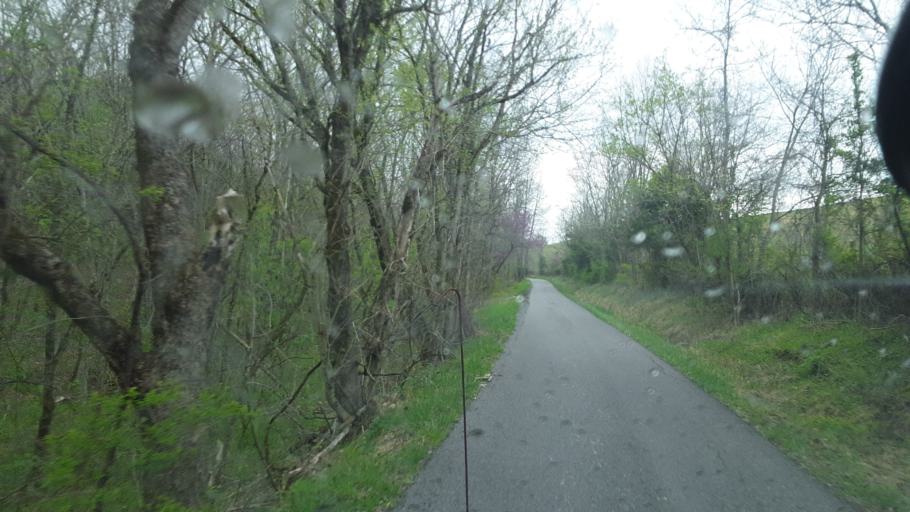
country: US
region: Kentucky
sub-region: Owen County
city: Owenton
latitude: 38.6432
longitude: -84.7816
